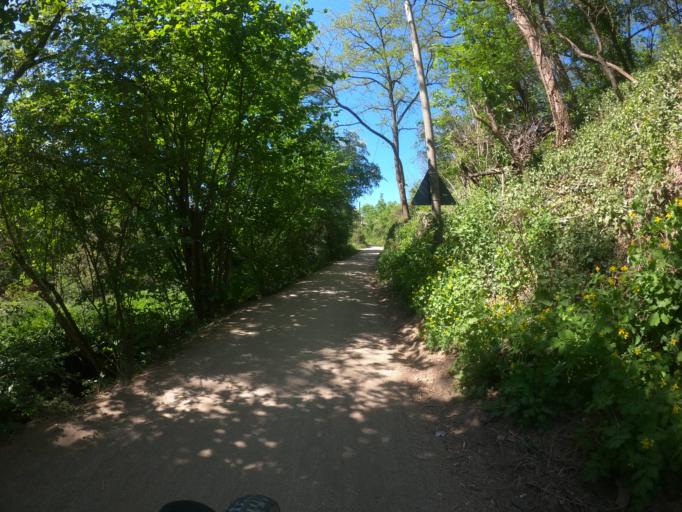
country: DE
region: Hesse
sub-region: Regierungsbezirk Darmstadt
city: Florsheim
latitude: 50.0072
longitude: 8.4013
